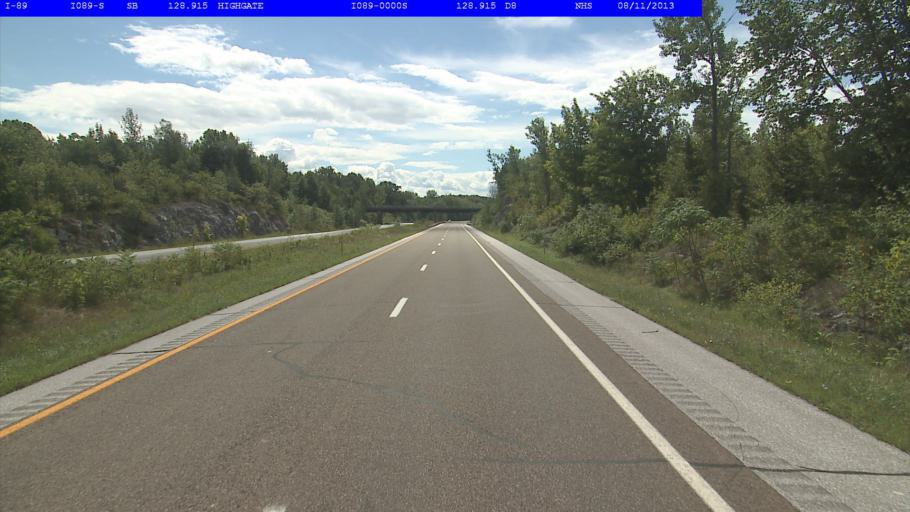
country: US
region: Vermont
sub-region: Franklin County
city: Swanton
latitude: 44.9963
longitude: -73.0861
